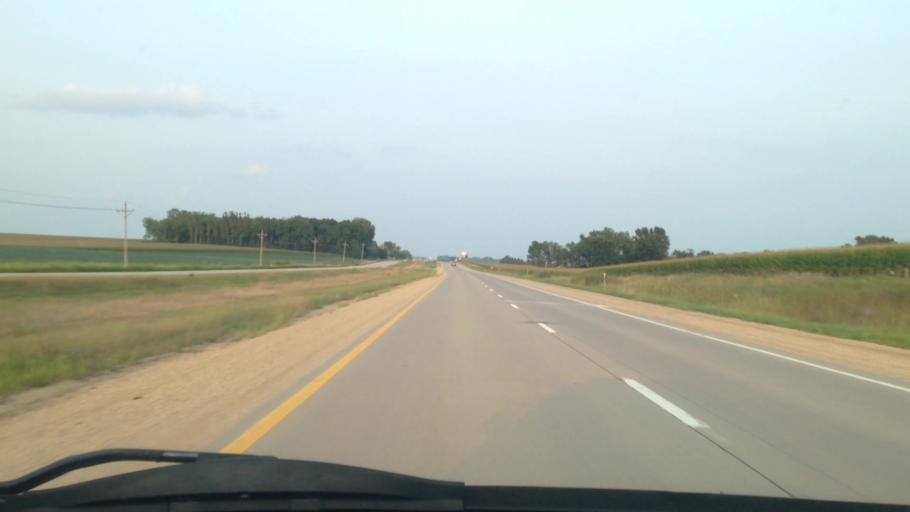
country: US
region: Iowa
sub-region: Benton County
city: Atkins
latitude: 41.9632
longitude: -91.8869
